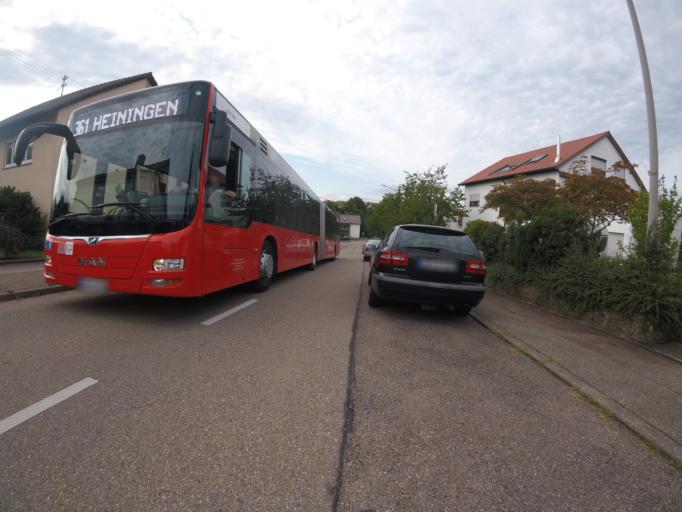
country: DE
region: Baden-Wuerttemberg
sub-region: Regierungsbezirk Stuttgart
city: Backnang
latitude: 48.9217
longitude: 9.4269
